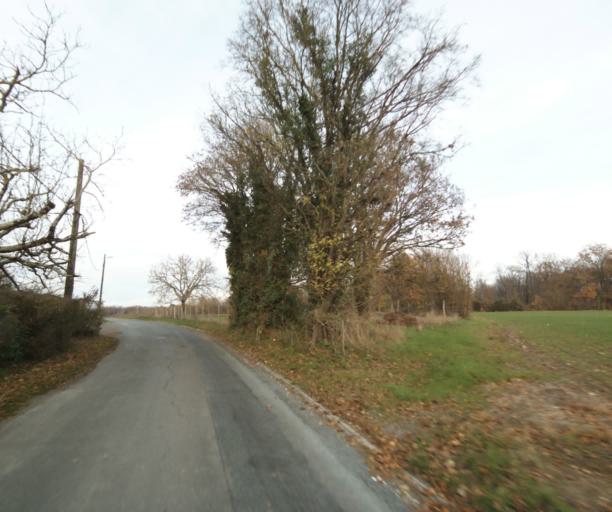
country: FR
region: Poitou-Charentes
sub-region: Departement de la Charente-Maritime
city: Fontcouverte
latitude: 45.8095
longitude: -0.5790
